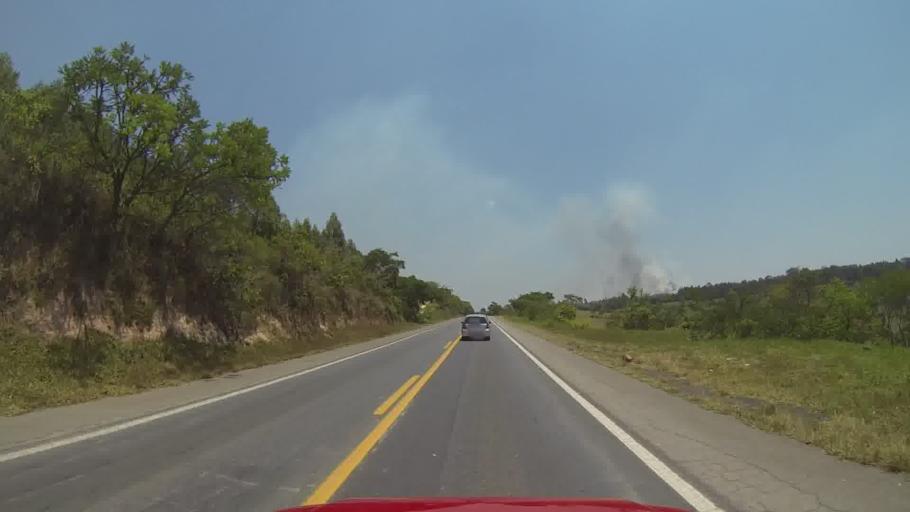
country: BR
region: Minas Gerais
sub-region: Itapecerica
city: Itapecerica
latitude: -20.3427
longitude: -45.2595
